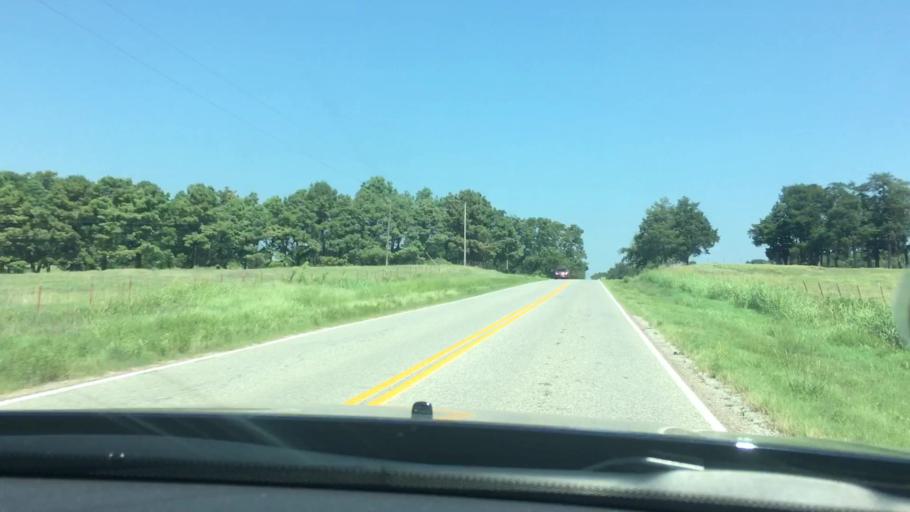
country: US
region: Oklahoma
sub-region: Johnston County
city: Tishomingo
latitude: 34.2603
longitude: -96.5487
